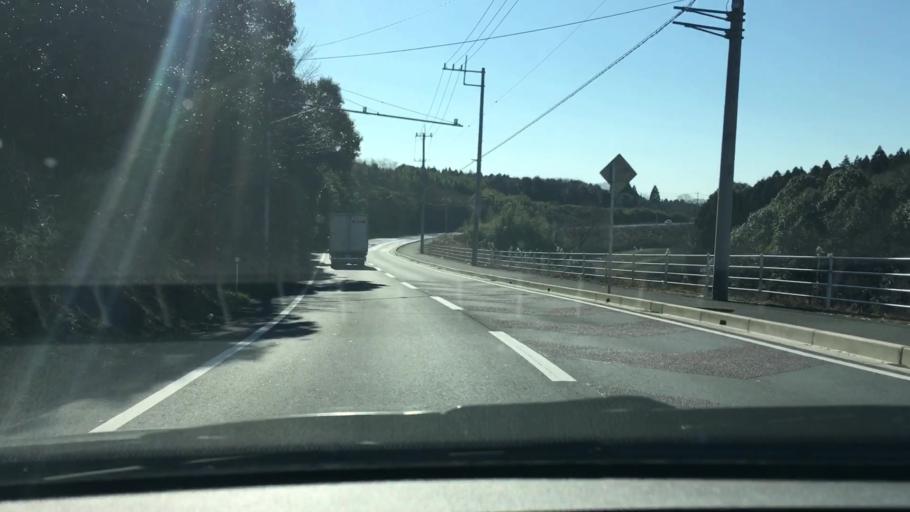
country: JP
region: Chiba
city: Narita
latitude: 35.7339
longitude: 140.4001
